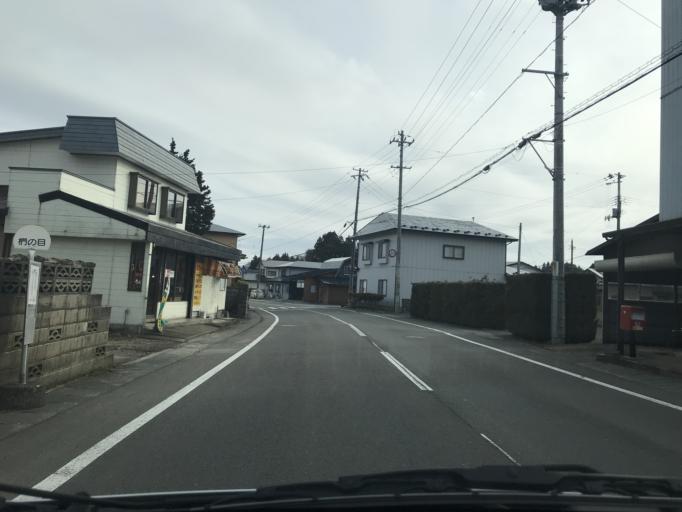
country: JP
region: Iwate
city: Hanamaki
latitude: 39.4247
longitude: 141.0847
